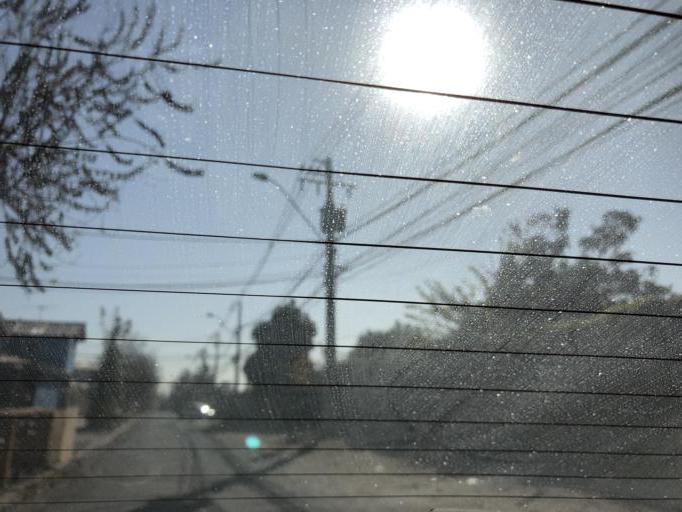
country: CL
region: Santiago Metropolitan
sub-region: Provincia de Santiago
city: La Pintana
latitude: -33.6192
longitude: -70.6241
